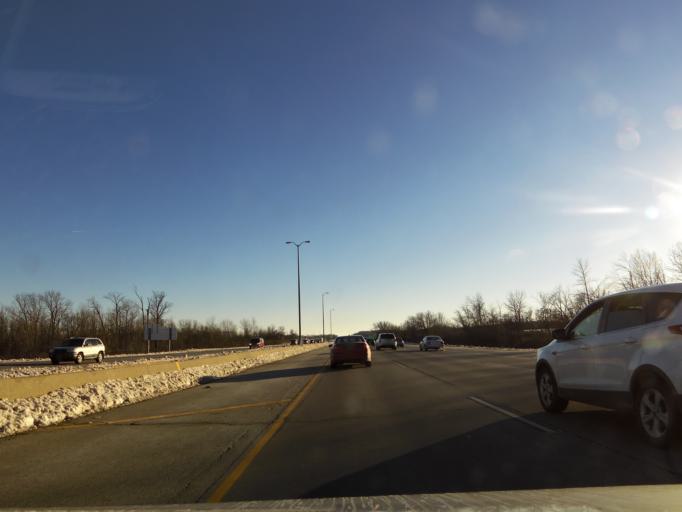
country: US
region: Wisconsin
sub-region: Milwaukee County
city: Greendale
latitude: 42.9105
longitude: -87.9360
